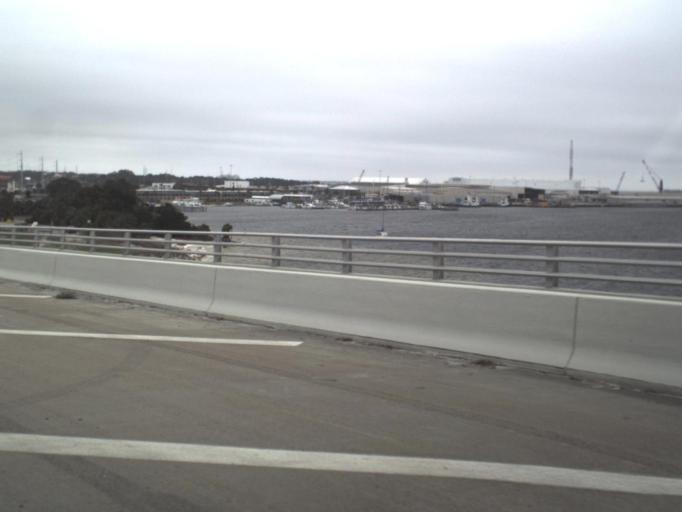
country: US
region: Florida
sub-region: Bay County
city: Upper Grand Lagoon
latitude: 30.1878
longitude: -85.7385
